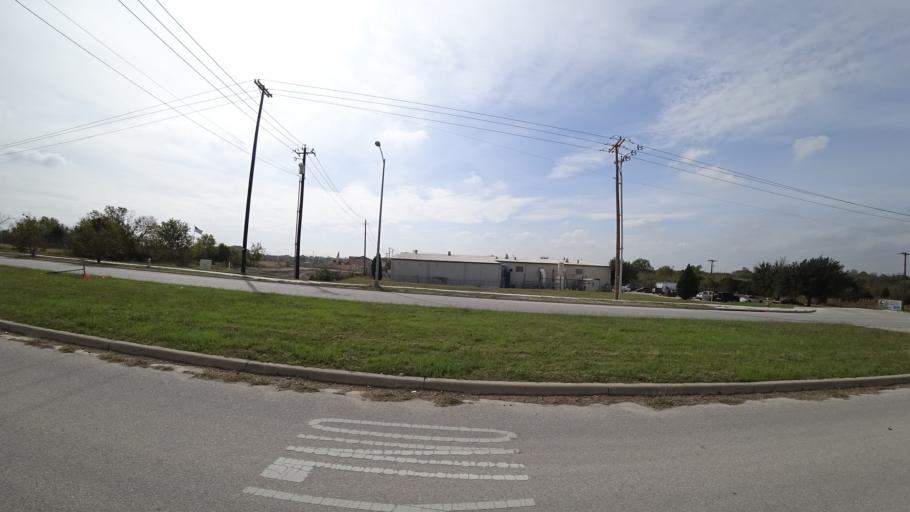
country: US
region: Texas
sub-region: Travis County
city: Windemere
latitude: 30.4371
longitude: -97.6571
